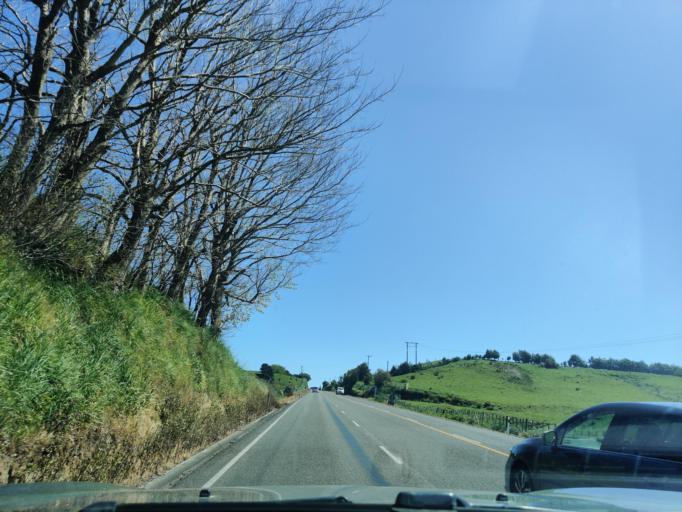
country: NZ
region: Taranaki
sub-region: South Taranaki District
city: Hawera
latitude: -39.6173
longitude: 174.3403
